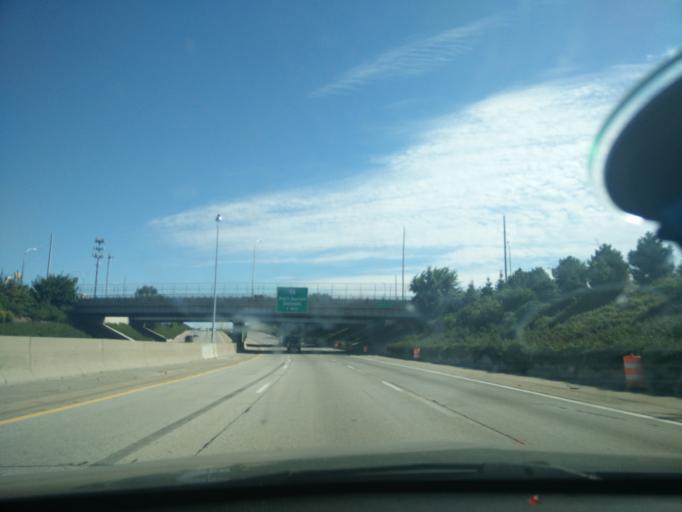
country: US
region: Michigan
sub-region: Macomb County
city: Roseville
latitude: 42.4944
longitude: -82.9401
